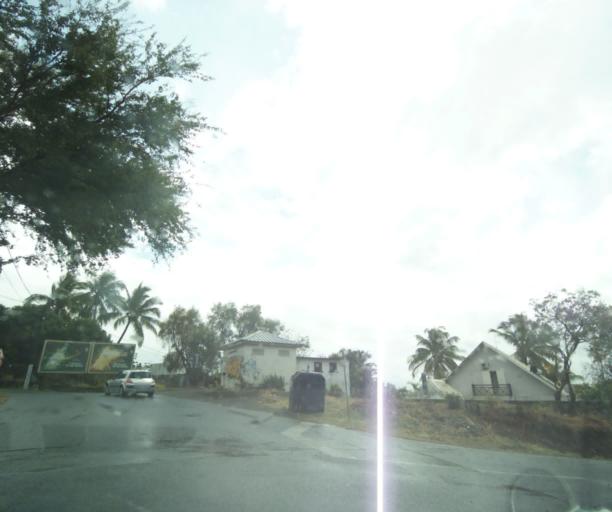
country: RE
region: Reunion
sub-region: Reunion
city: La Possession
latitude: -20.9767
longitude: 55.3288
